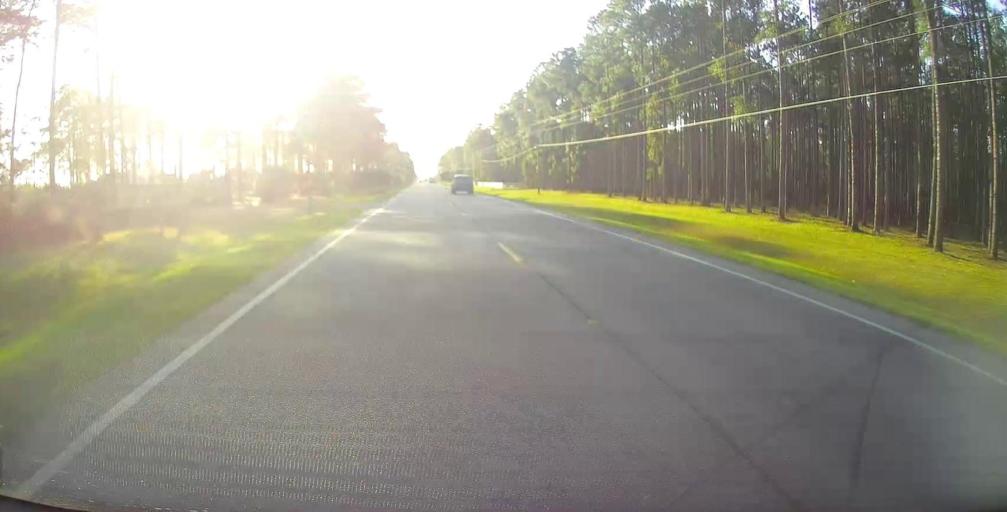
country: US
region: Georgia
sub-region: Evans County
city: Claxton
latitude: 32.1497
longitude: -81.9810
